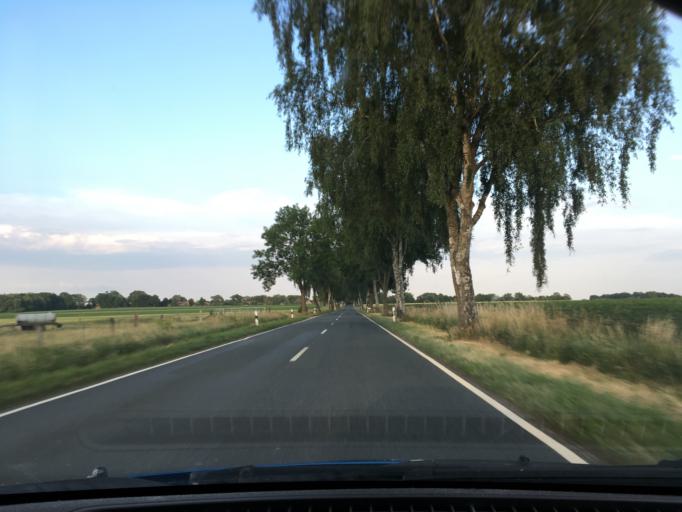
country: DE
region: Lower Saxony
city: Scharnhorst
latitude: 52.7212
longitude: 10.3022
